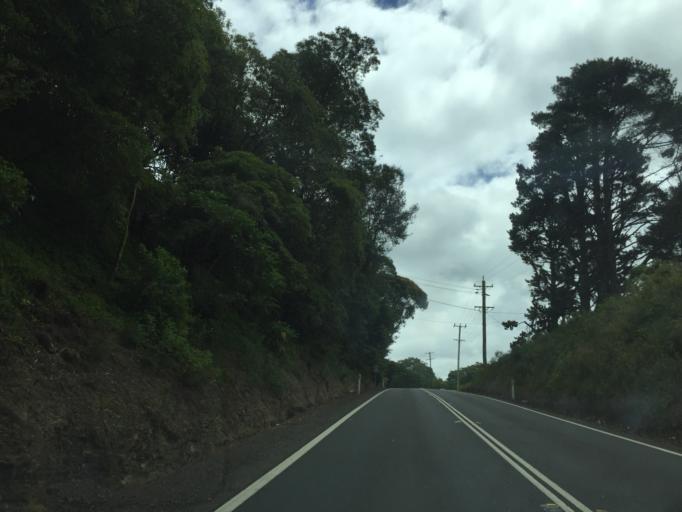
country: AU
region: New South Wales
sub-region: Hawkesbury
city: Richmond
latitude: -33.5213
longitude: 150.6279
